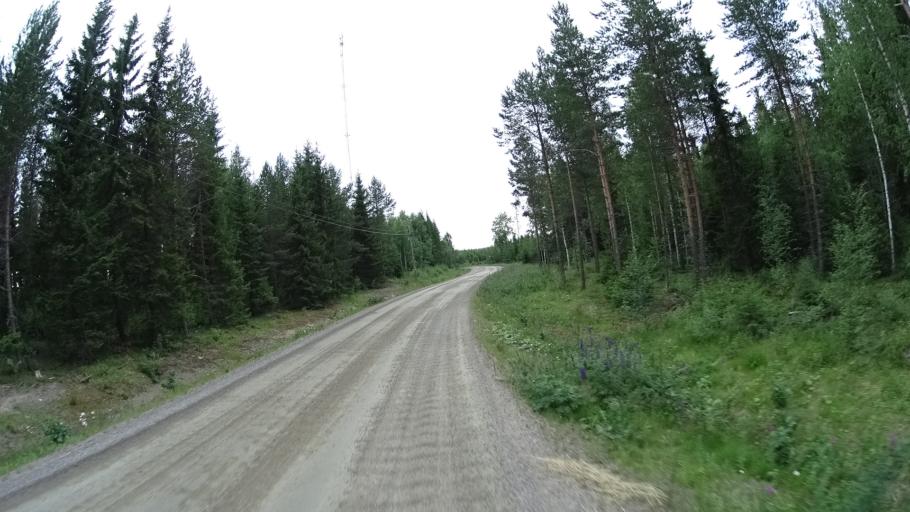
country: FI
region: Satakunta
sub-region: Pohjois-Satakunta
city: Jaemijaervi
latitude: 61.7761
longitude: 22.8623
